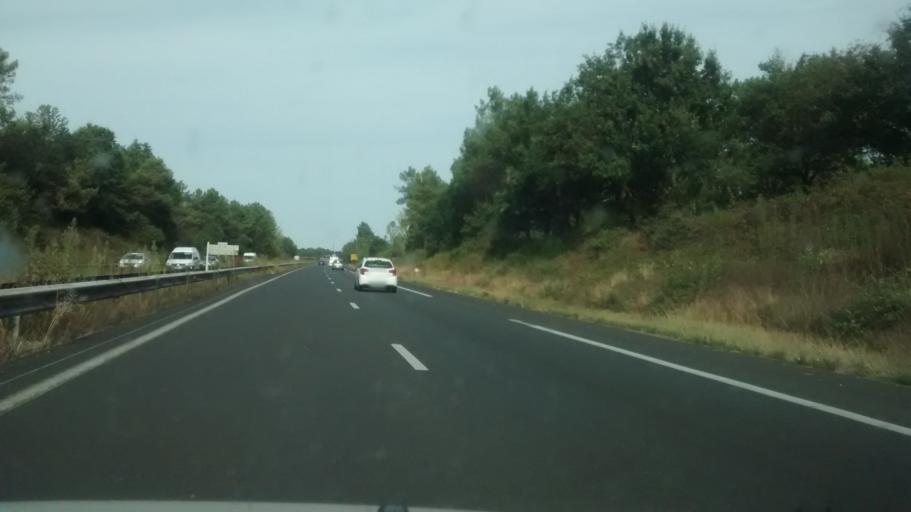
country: FR
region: Aquitaine
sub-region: Departement du Lot-et-Garonne
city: Meilhan-sur-Garonne
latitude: 44.5015
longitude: -0.0320
